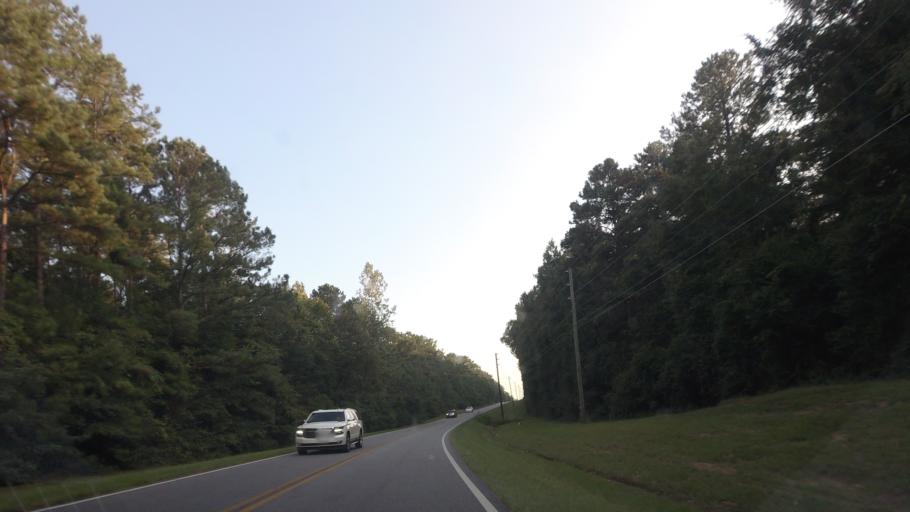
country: US
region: Georgia
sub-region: Bibb County
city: West Point
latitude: 32.8760
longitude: -83.7803
